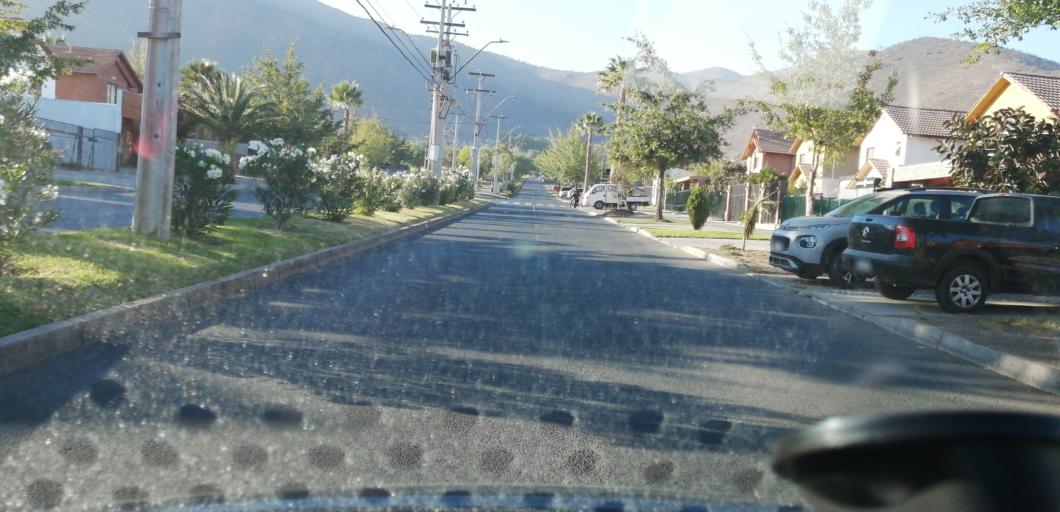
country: CL
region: Santiago Metropolitan
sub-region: Provincia de Santiago
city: Lo Prado
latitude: -33.4531
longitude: -70.8486
